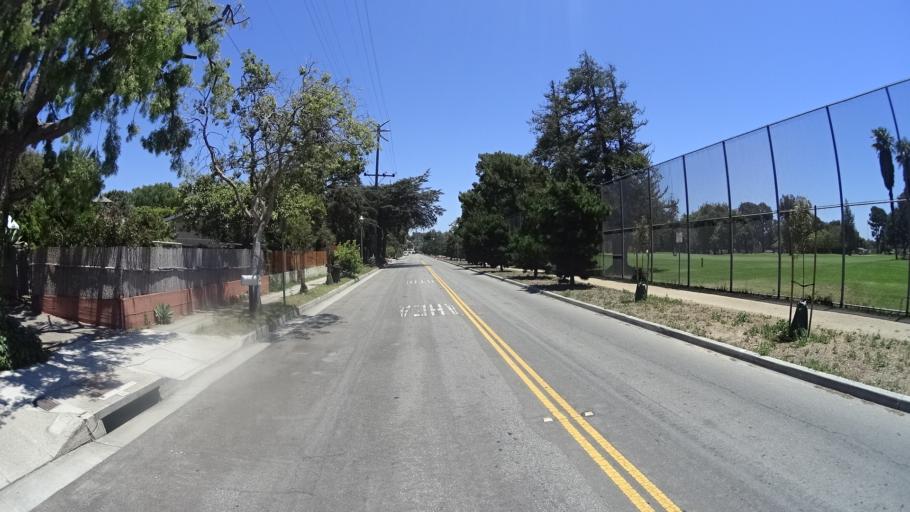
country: US
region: California
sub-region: Los Angeles County
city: Marina del Rey
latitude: 34.0082
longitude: -118.4596
